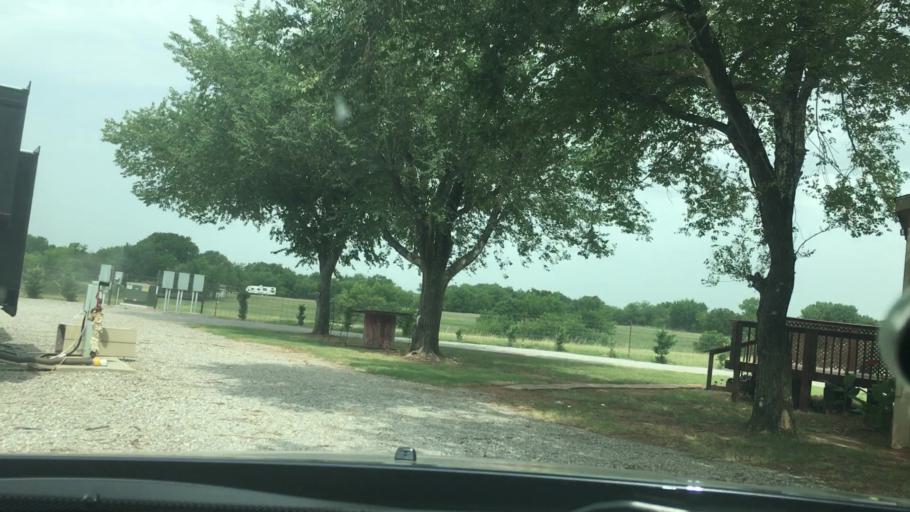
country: US
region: Oklahoma
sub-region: Garvin County
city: Pauls Valley
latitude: 34.8472
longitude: -97.2794
